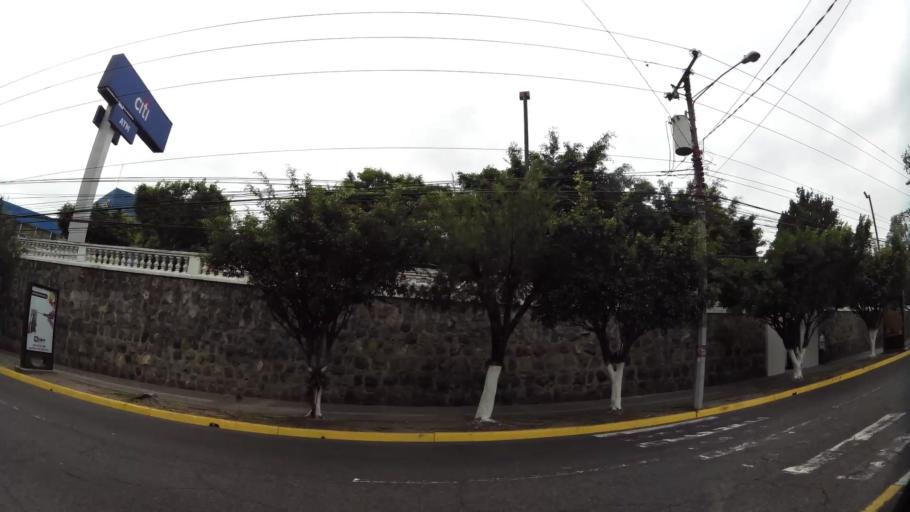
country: SV
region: San Salvador
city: Mejicanos
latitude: 13.7015
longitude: -89.2264
